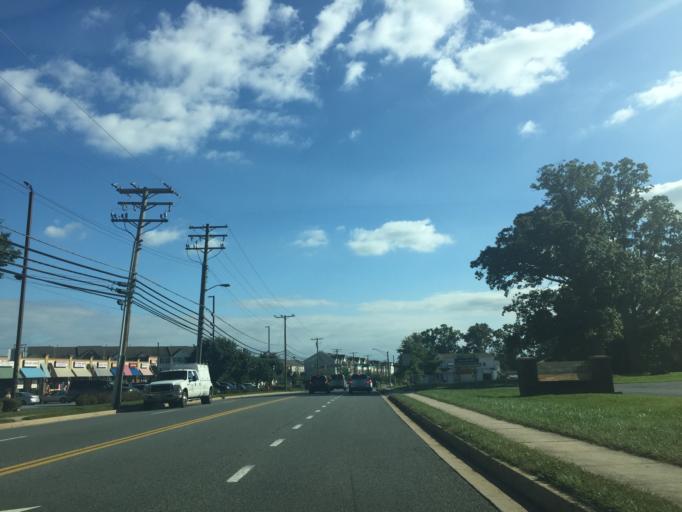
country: US
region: Maryland
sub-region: Baltimore County
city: Middle River
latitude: 39.3496
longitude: -76.4509
